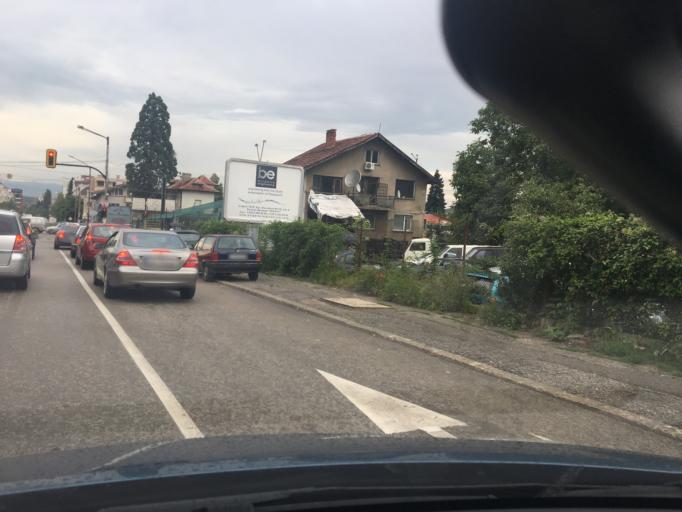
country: BG
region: Sofia-Capital
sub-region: Stolichna Obshtina
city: Sofia
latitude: 42.6594
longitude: 23.2649
